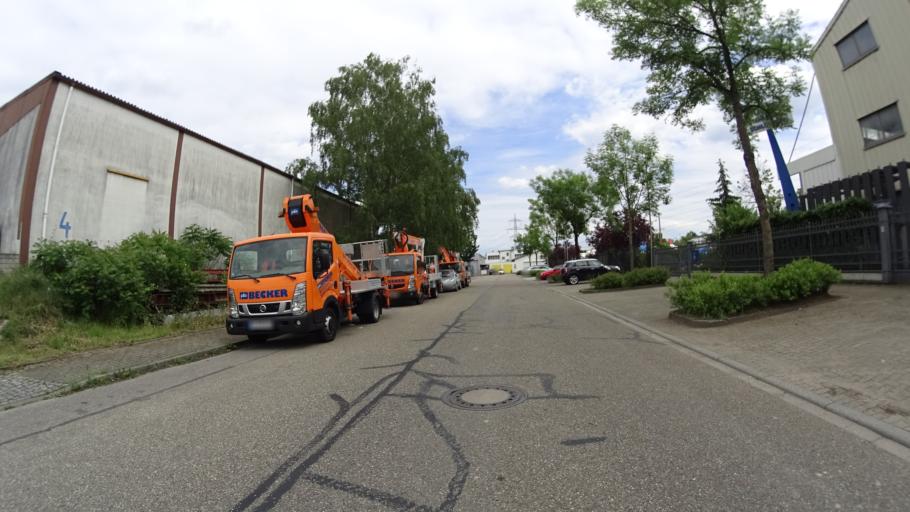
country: DE
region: Baden-Wuerttemberg
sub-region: Karlsruhe Region
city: Rheinstetten
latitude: 49.0103
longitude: 8.3176
